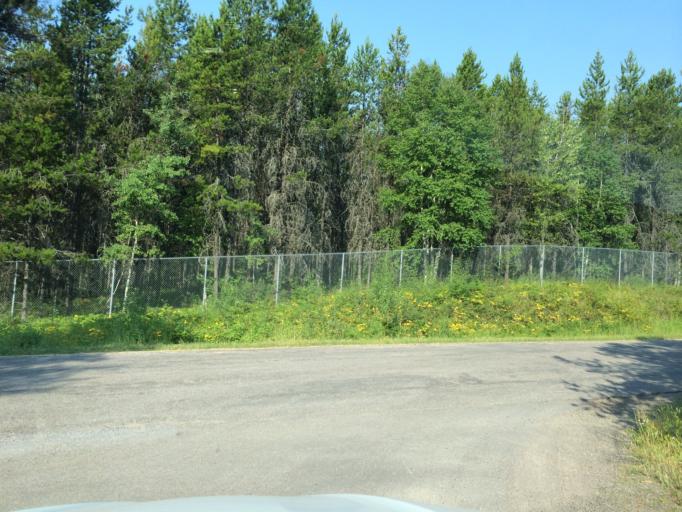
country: US
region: Montana
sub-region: Flathead County
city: Columbia Falls
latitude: 48.4757
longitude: -114.0011
